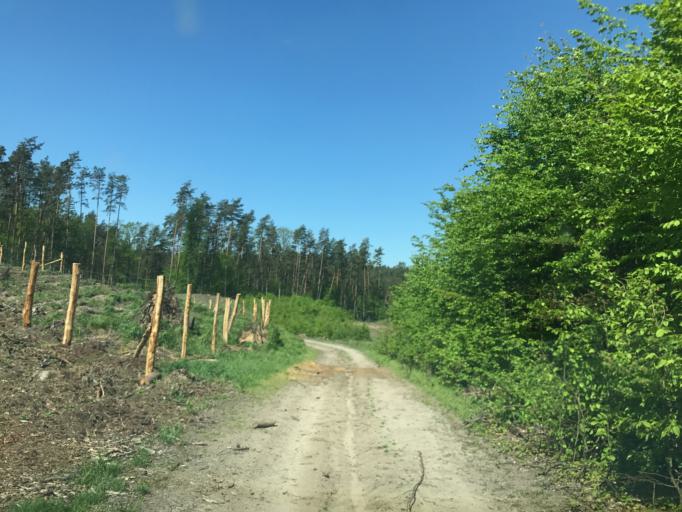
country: PL
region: Kujawsko-Pomorskie
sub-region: Powiat brodnicki
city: Gorzno
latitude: 53.2103
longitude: 19.6953
